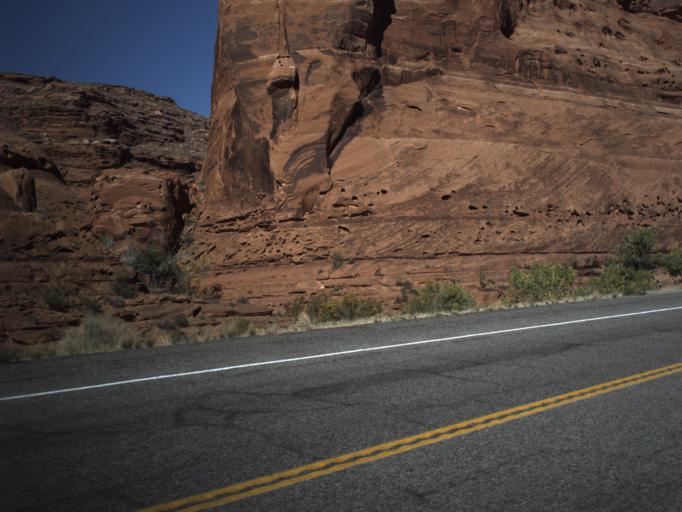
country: US
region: Utah
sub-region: San Juan County
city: Blanding
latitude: 37.9643
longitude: -110.4924
